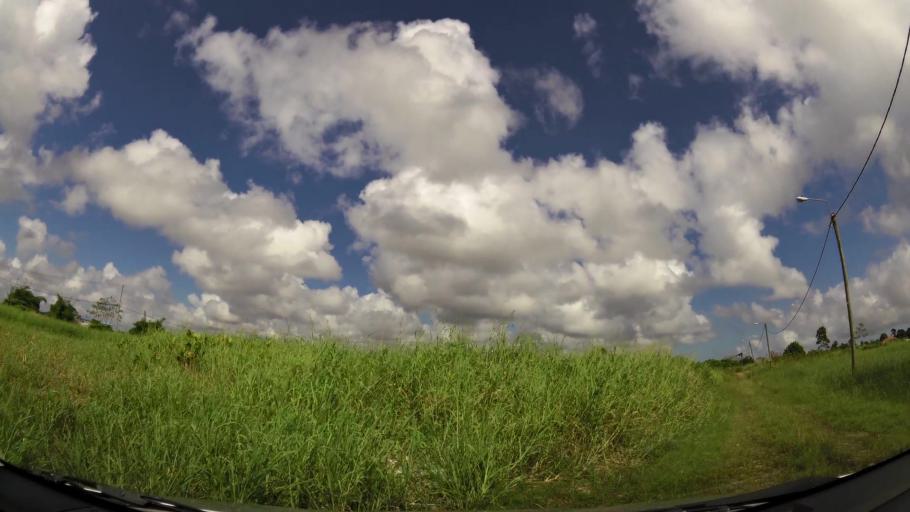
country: SR
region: Commewijne
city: Nieuw Amsterdam
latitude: 5.8693
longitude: -55.1223
